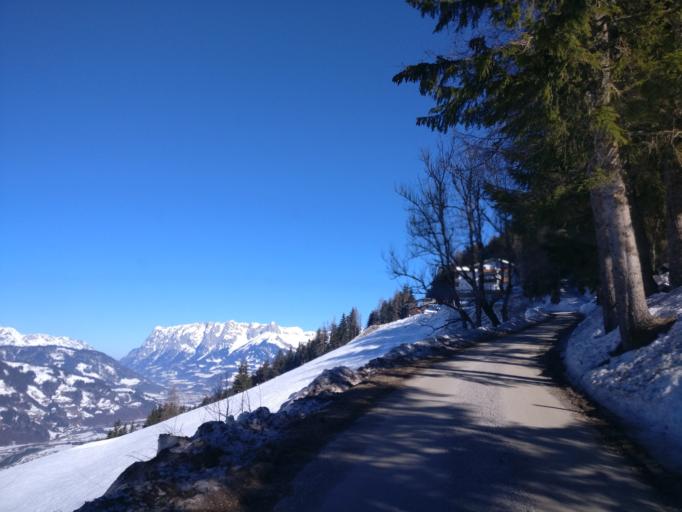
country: AT
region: Salzburg
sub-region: Politischer Bezirk Sankt Johann im Pongau
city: Sankt Johann im Pongau
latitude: 47.3392
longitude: 13.2242
